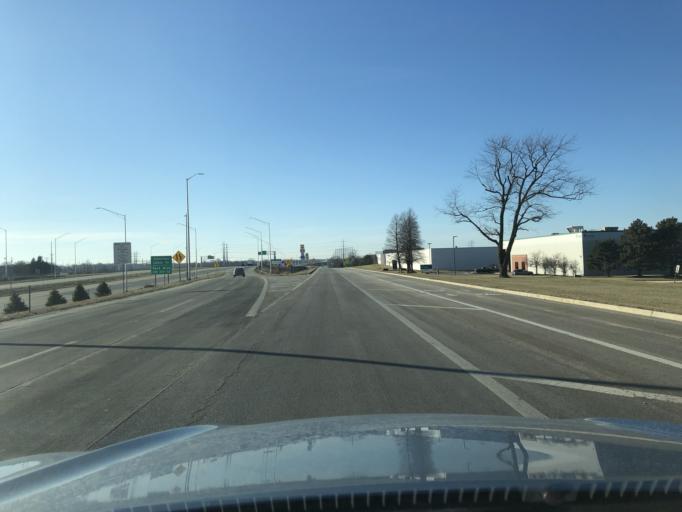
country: US
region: Illinois
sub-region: DuPage County
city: Wood Dale
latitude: 41.9842
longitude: -87.9818
